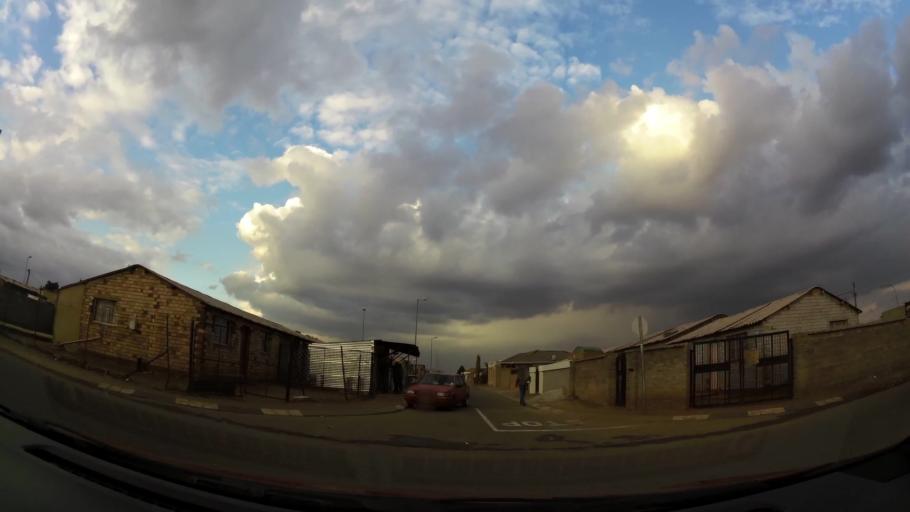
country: ZA
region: Gauteng
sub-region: City of Johannesburg Metropolitan Municipality
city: Soweto
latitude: -26.2481
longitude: 27.8278
